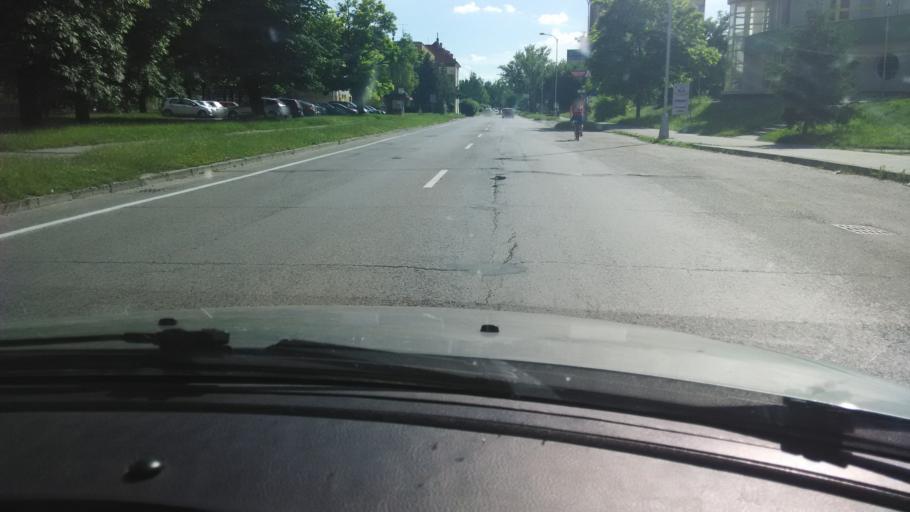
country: SK
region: Nitriansky
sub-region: Okres Nove Zamky
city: Nove Zamky
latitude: 47.9916
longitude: 18.1653
